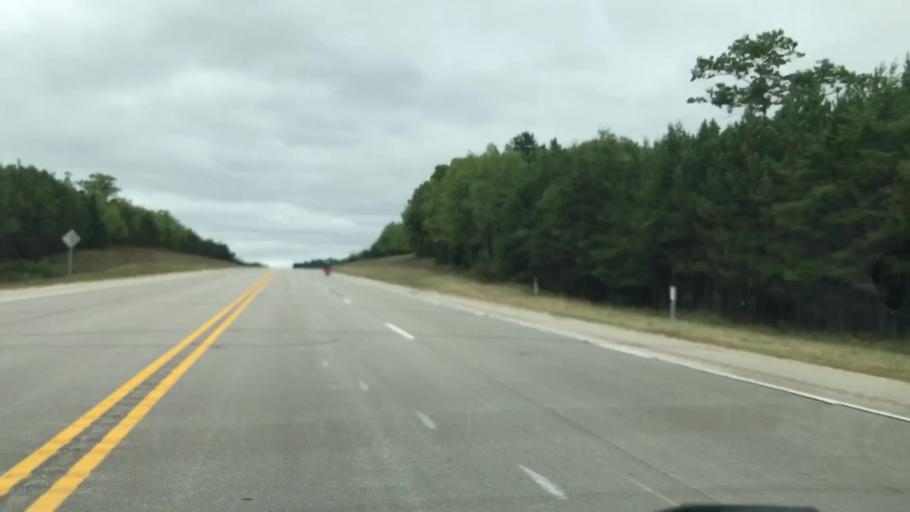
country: US
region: Michigan
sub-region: Schoolcraft County
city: Manistique
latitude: 45.9073
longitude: -86.4159
